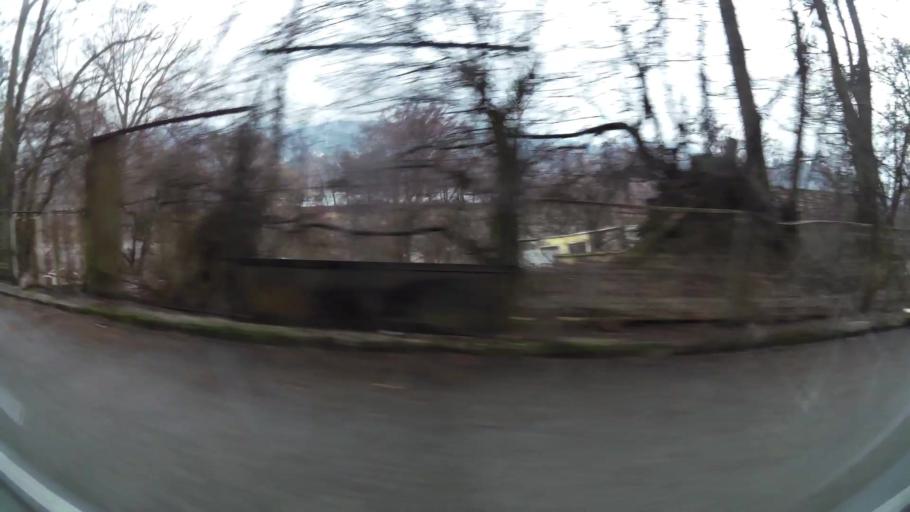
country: BG
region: Sofia-Capital
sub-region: Stolichna Obshtina
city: Sofia
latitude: 42.5890
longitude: 23.4250
